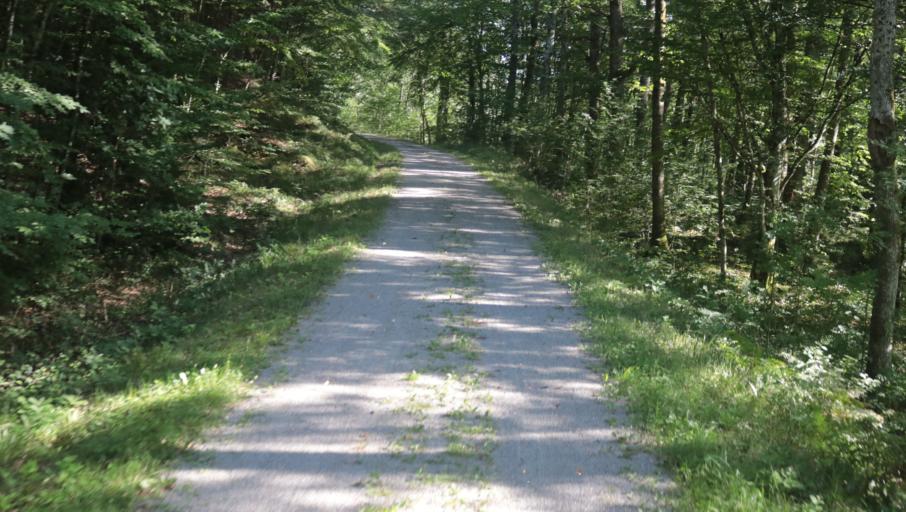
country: SE
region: Blekinge
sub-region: Karlshamns Kommun
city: Svangsta
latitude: 56.3609
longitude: 14.6894
